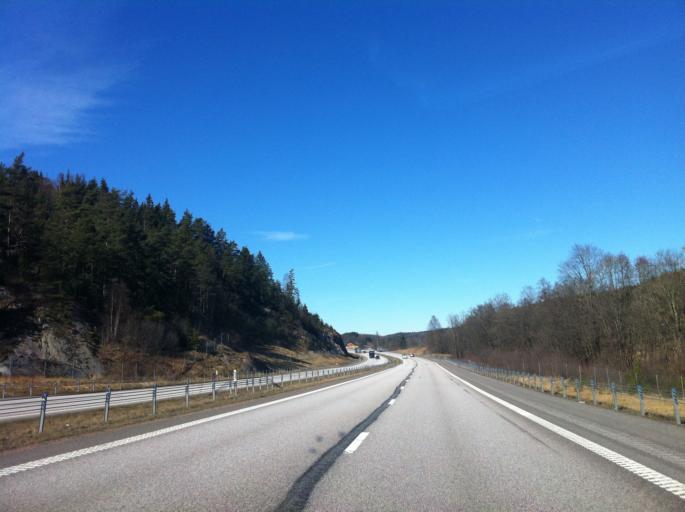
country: SE
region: Vaestra Goetaland
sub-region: Munkedals Kommun
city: Munkedal
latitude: 58.3731
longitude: 11.7866
